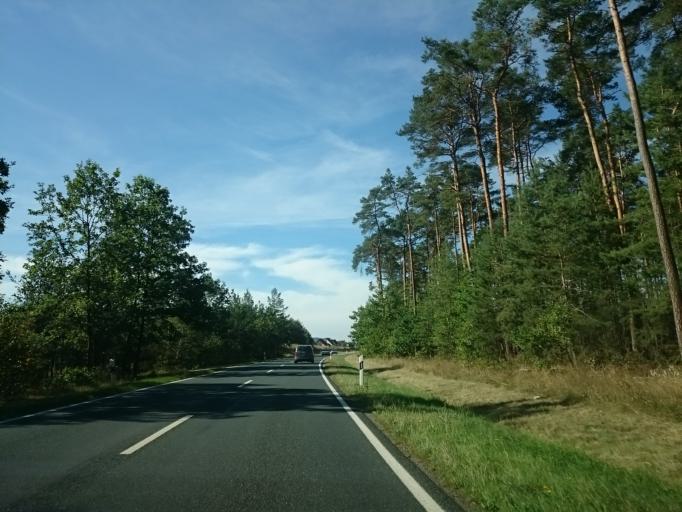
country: DE
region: Bavaria
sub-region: Regierungsbezirk Mittelfranken
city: Heideck
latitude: 49.1473
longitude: 11.1570
